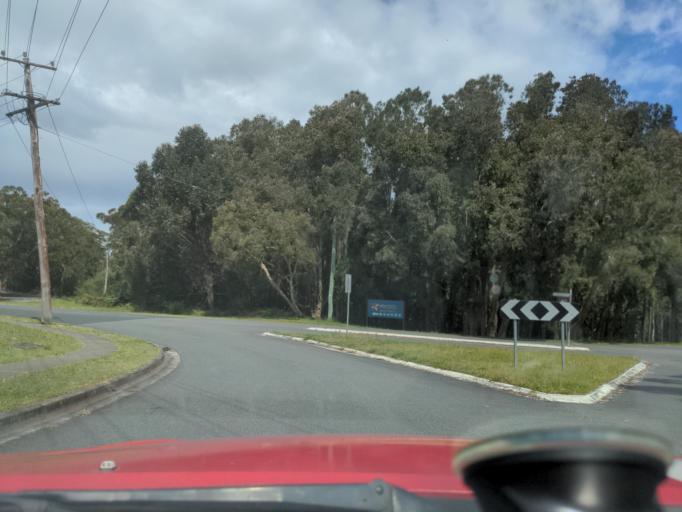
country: AU
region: New South Wales
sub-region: Great Lakes
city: Hawks Nest
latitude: -32.6766
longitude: 152.1765
